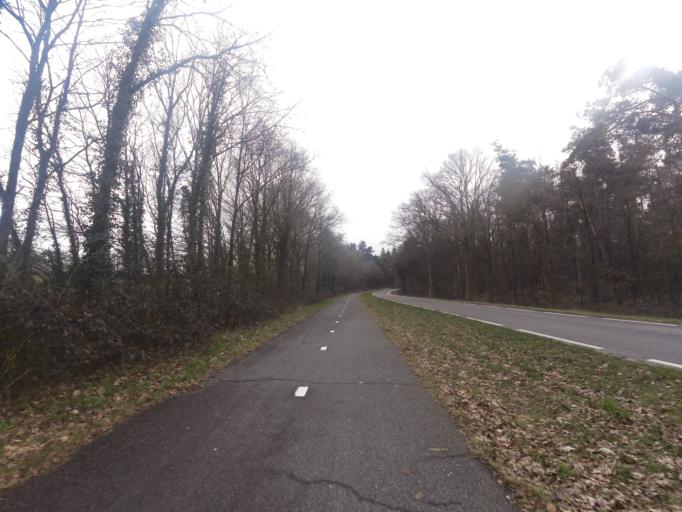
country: NL
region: Gelderland
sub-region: Gemeente Doetinchem
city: Doetinchem
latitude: 51.9489
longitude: 6.3341
